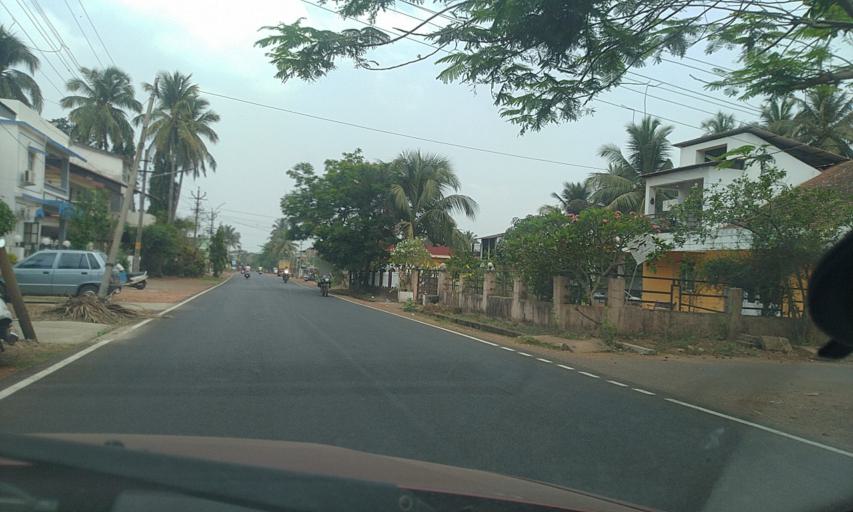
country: IN
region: Goa
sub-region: North Goa
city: Mapuca
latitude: 15.6053
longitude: 73.8046
